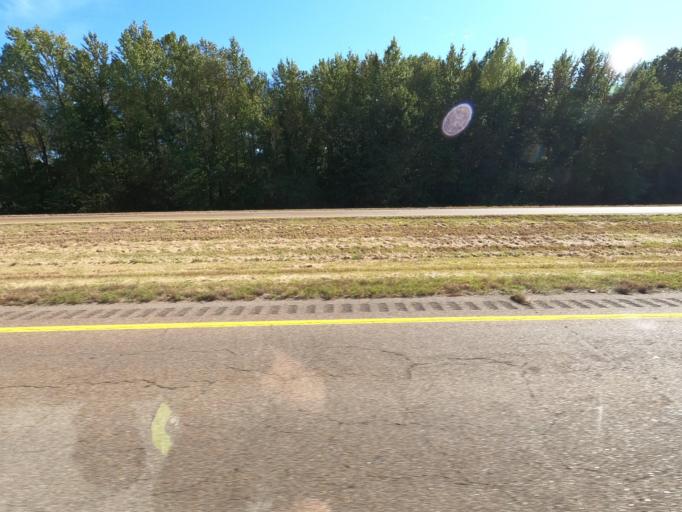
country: US
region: Tennessee
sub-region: Obion County
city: South Fulton
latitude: 36.4860
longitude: -88.9335
